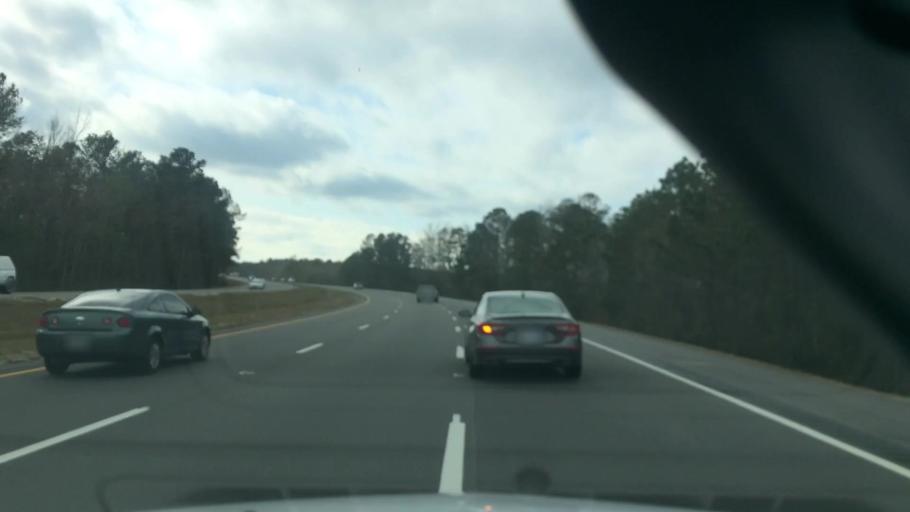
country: US
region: North Carolina
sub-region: New Hanover County
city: Skippers Corner
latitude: 34.3179
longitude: -77.8833
